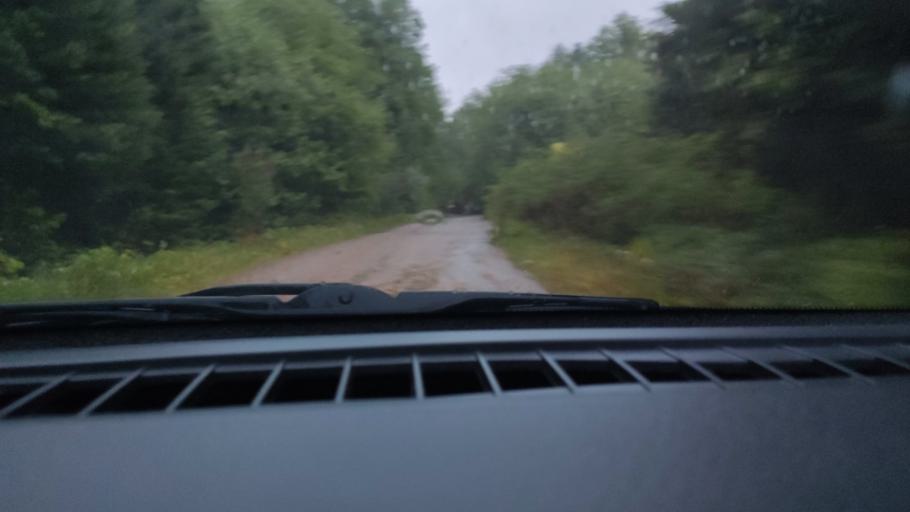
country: RU
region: Perm
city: Perm
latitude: 58.0976
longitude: 56.4132
